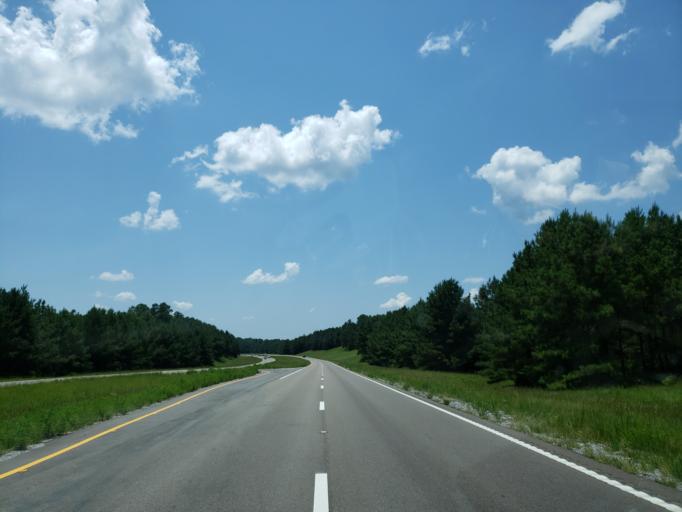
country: US
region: Mississippi
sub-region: Clarke County
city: Stonewall
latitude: 32.2050
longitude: -88.7031
